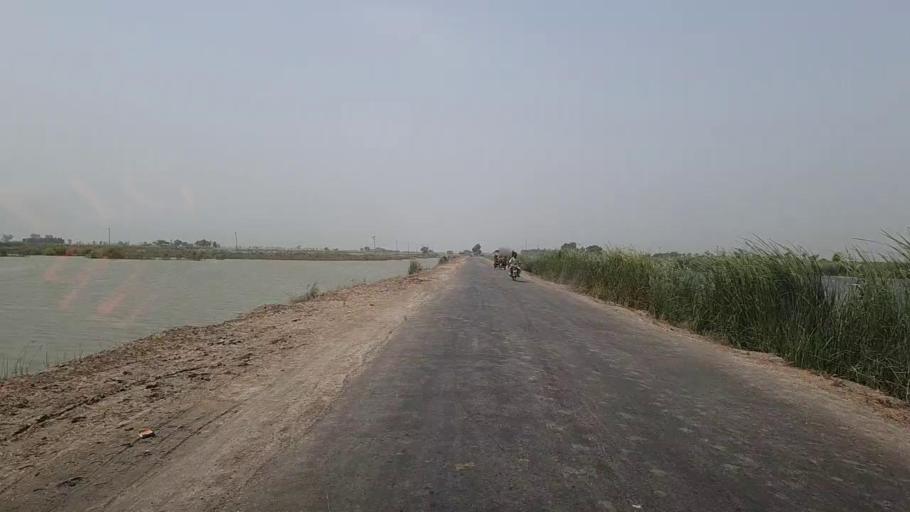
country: PK
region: Sindh
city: Radhan
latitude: 27.1505
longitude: 67.9384
